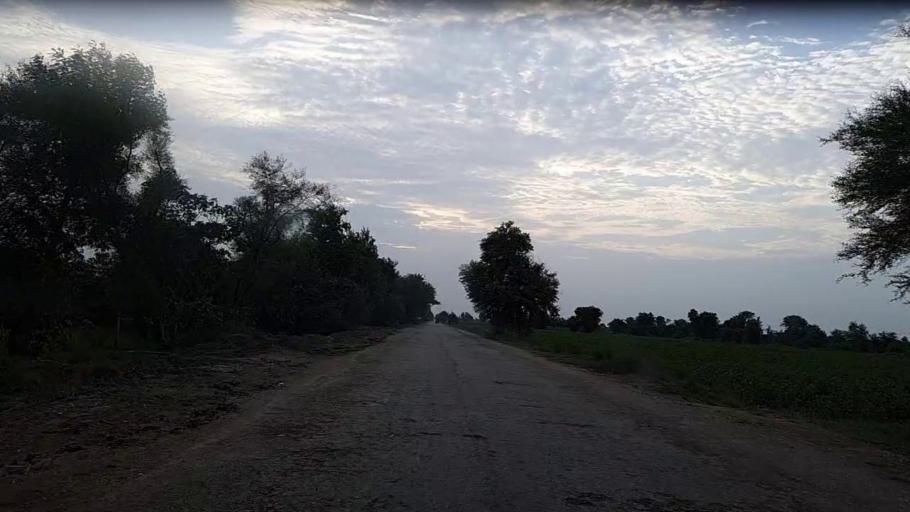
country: PK
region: Sindh
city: Pad Idan
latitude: 26.8022
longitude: 68.2211
